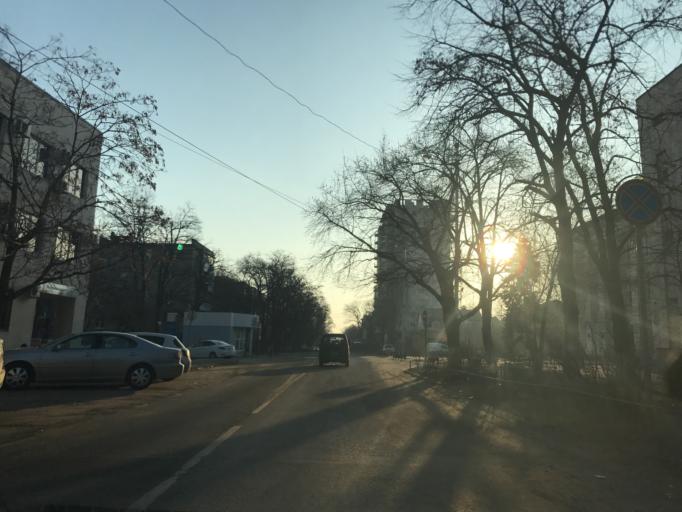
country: RU
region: Rostov
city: Rostov-na-Donu
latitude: 47.2144
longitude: 39.6787
